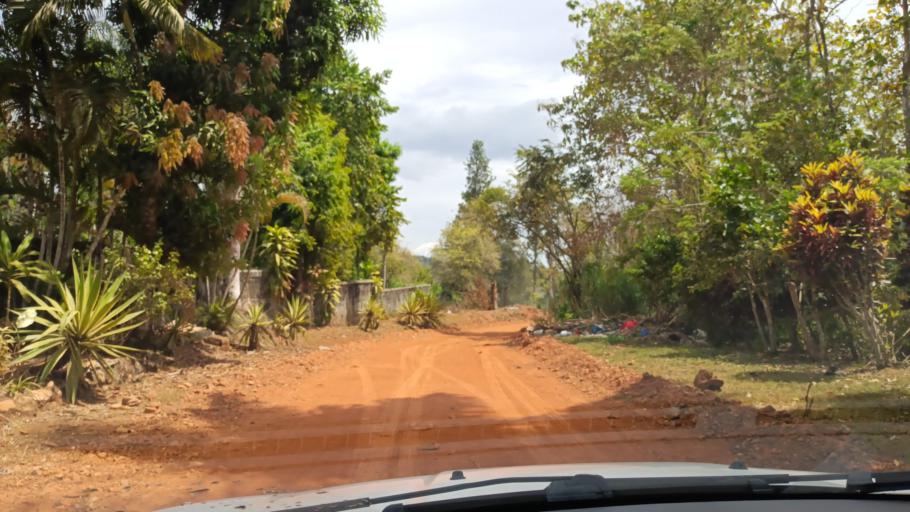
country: PA
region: Panama
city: La Cabima
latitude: 9.1300
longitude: -79.4994
